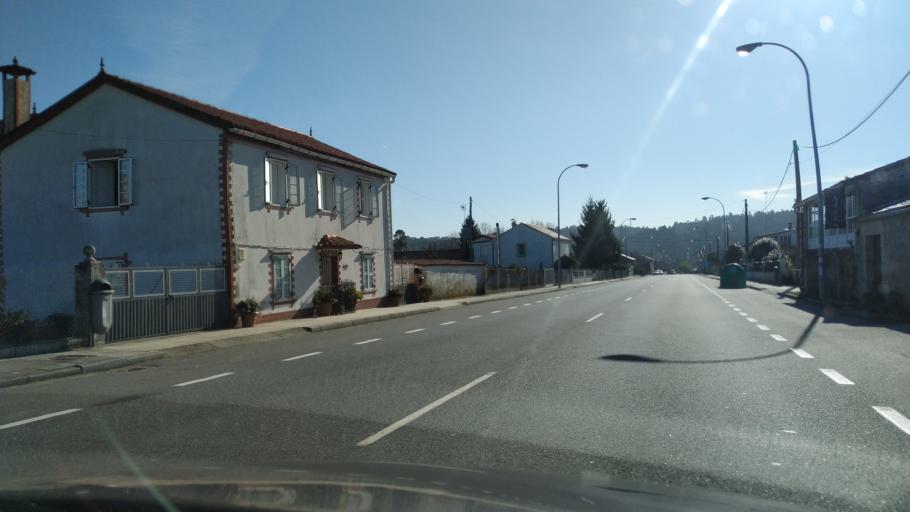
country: ES
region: Galicia
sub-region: Provincia de Pontevedra
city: Silleda
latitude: 42.7376
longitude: -8.3255
